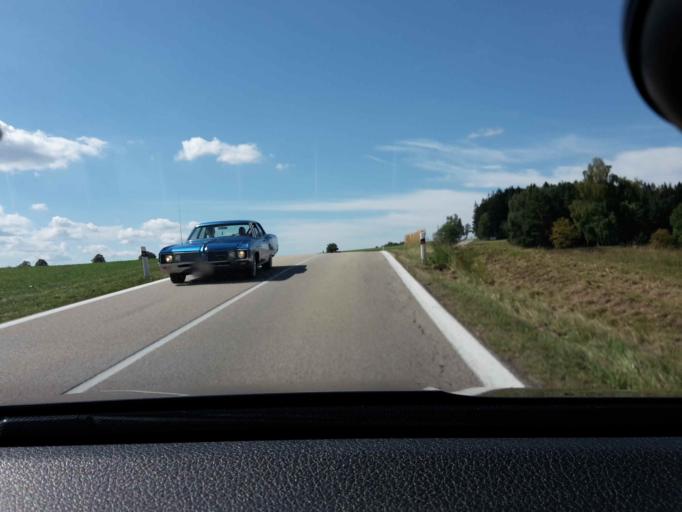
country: CZ
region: Jihocesky
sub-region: Okres Jindrichuv Hradec
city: Studena
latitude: 49.1691
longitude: 15.2507
